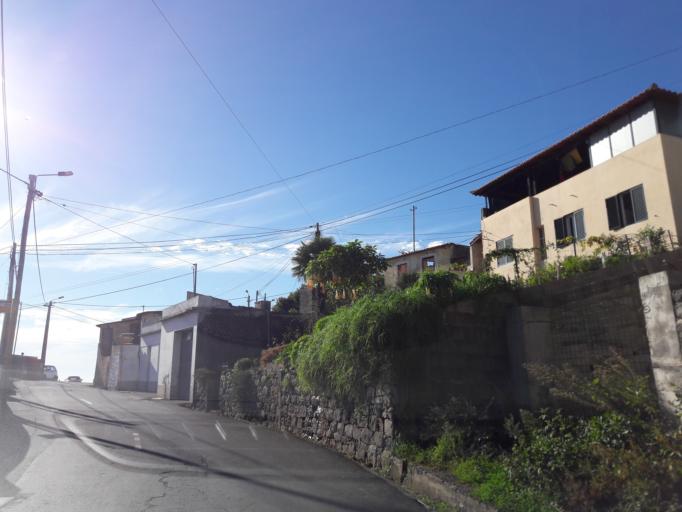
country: PT
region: Madeira
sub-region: Funchal
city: Nossa Senhora do Monte
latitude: 32.6786
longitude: -16.9104
